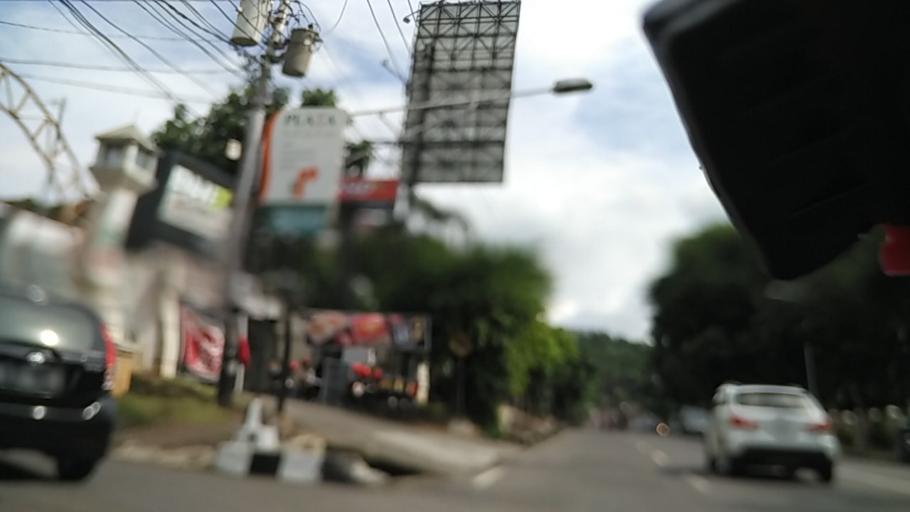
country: ID
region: Central Java
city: Semarang
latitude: -7.0211
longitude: 110.4198
